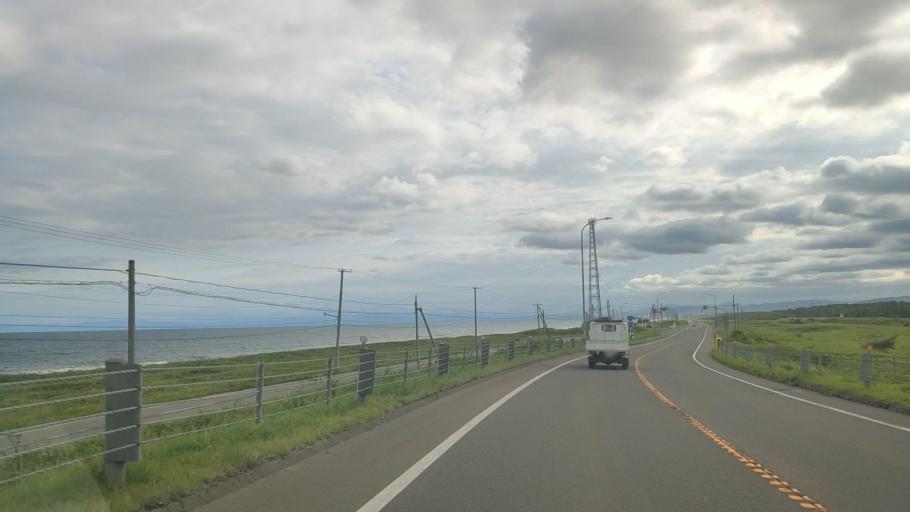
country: JP
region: Hokkaido
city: Niseko Town
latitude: 42.5784
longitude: 140.4541
